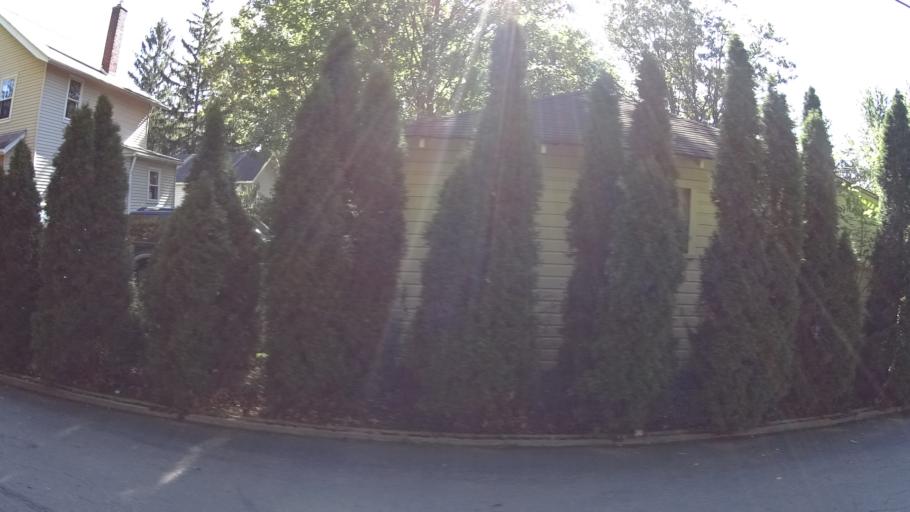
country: US
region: Ohio
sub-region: Lorain County
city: Lorain
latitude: 41.4339
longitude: -82.1662
